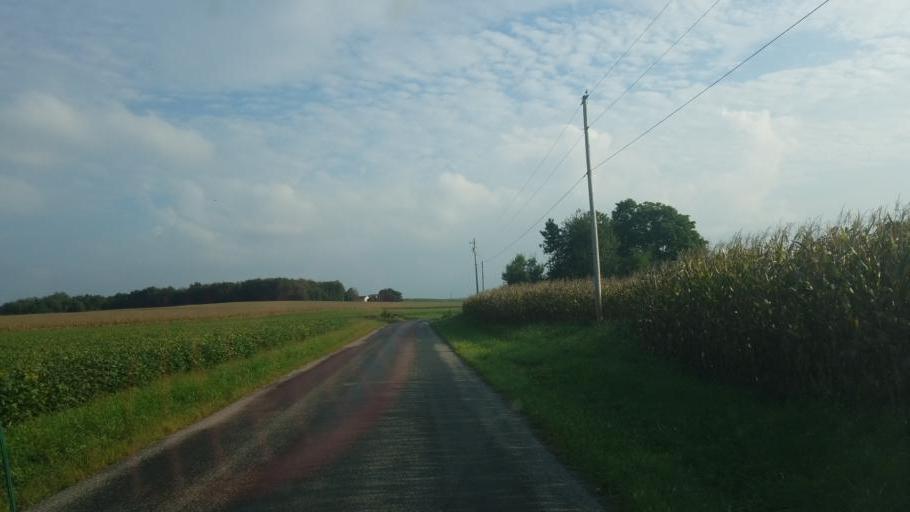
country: US
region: Ohio
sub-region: Wayne County
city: Wooster
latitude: 40.8859
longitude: -82.0217
